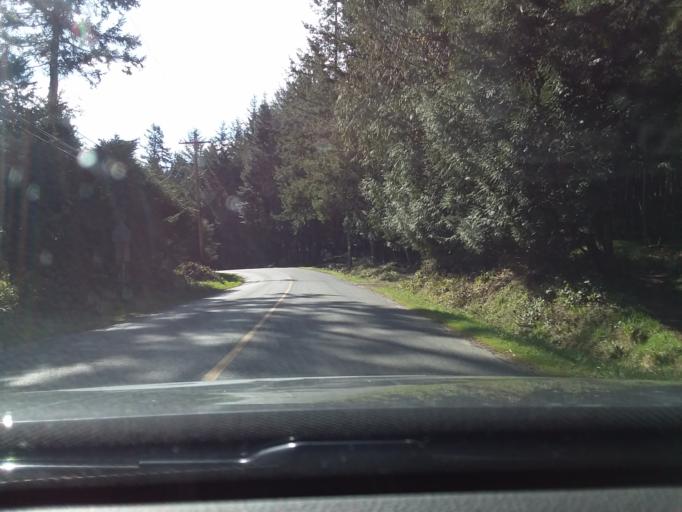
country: CA
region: British Columbia
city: North Saanich
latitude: 48.8843
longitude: -123.3309
